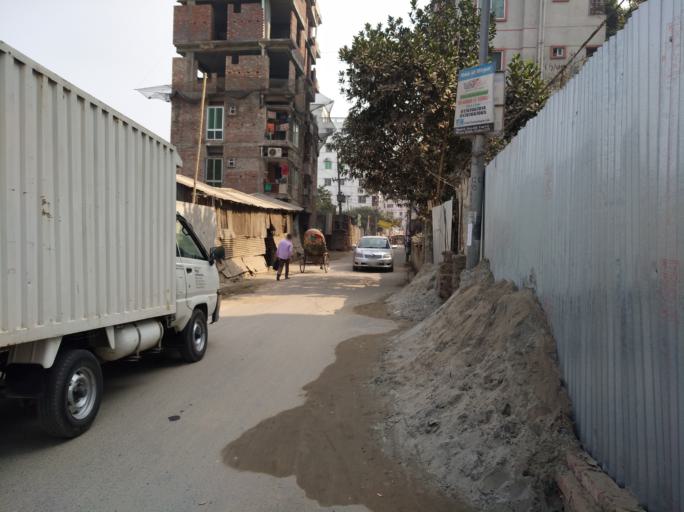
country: BD
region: Dhaka
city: Tungi
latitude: 23.8283
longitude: 90.3601
